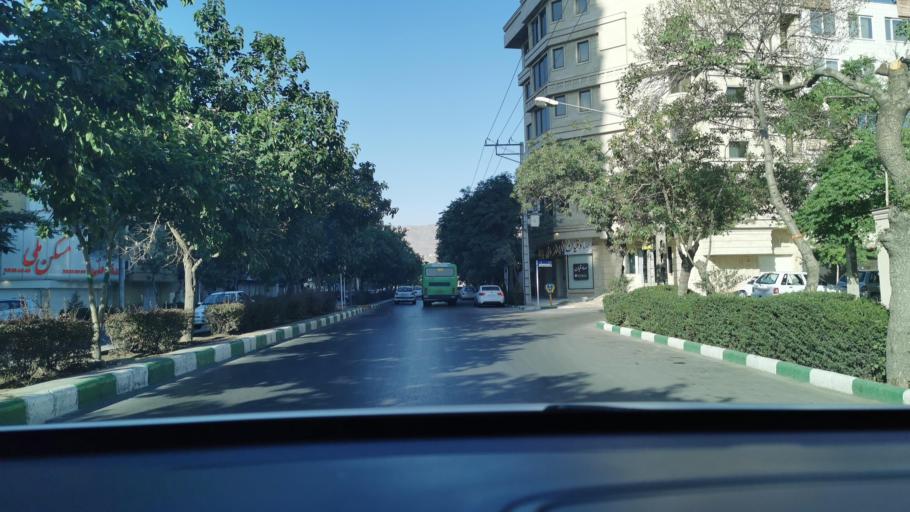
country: IR
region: Razavi Khorasan
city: Mashhad
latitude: 36.3147
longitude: 59.5178
